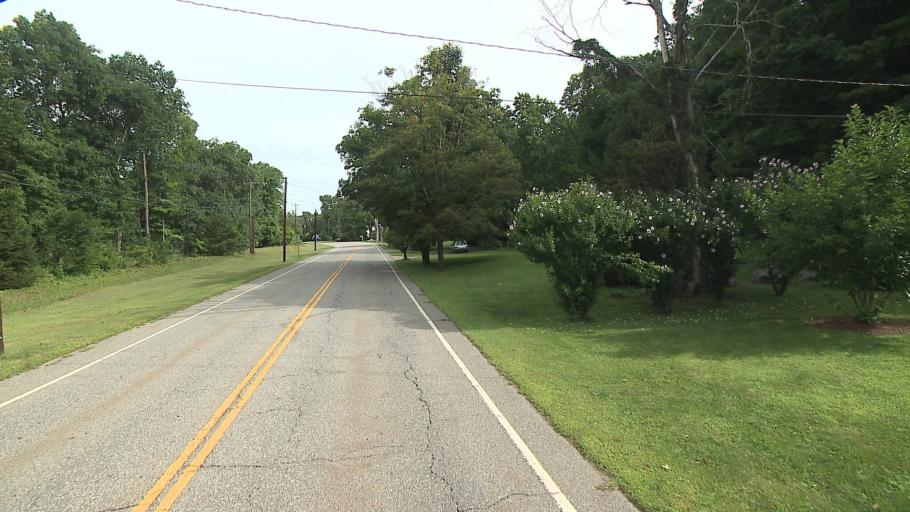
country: US
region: Connecticut
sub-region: Litchfield County
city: New Preston
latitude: 41.6482
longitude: -73.3170
